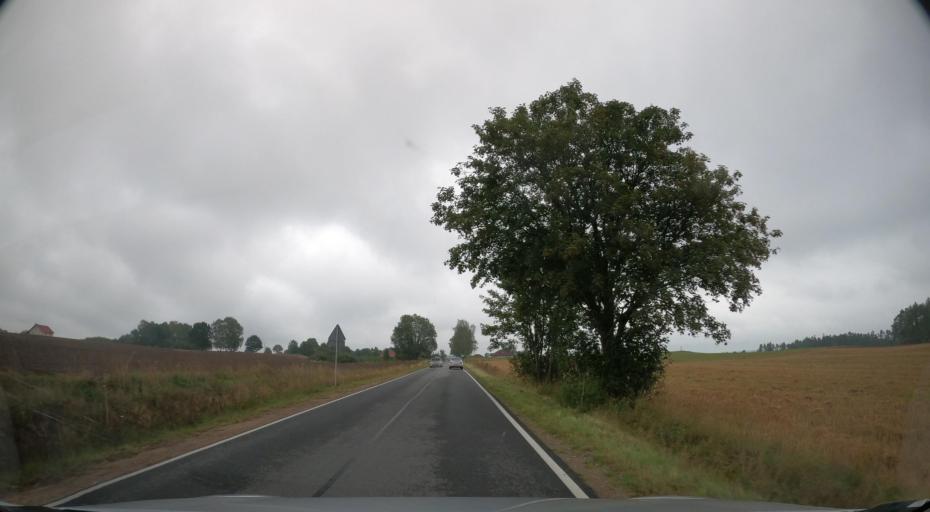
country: PL
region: Pomeranian Voivodeship
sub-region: Powiat wejherowski
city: Linia
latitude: 54.4841
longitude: 17.8485
